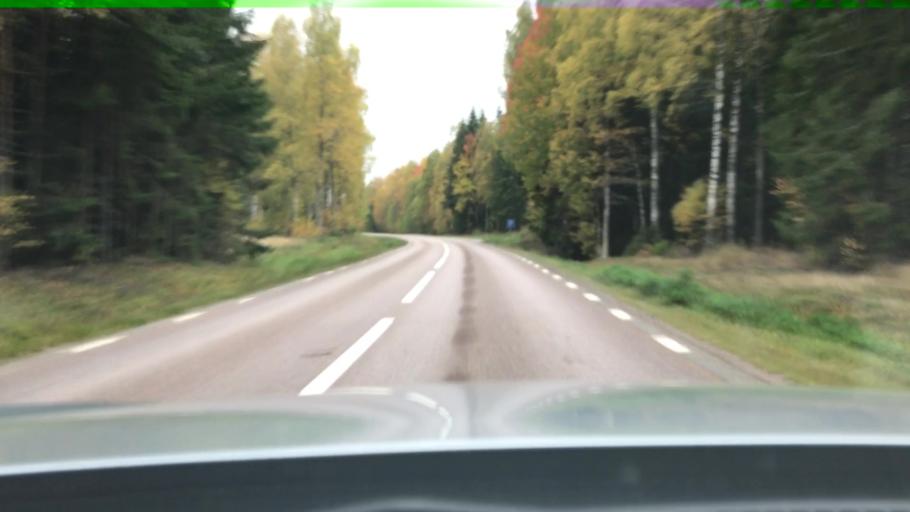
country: SE
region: Vaermland
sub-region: Eda Kommun
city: Amotfors
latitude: 59.7359
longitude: 12.2138
